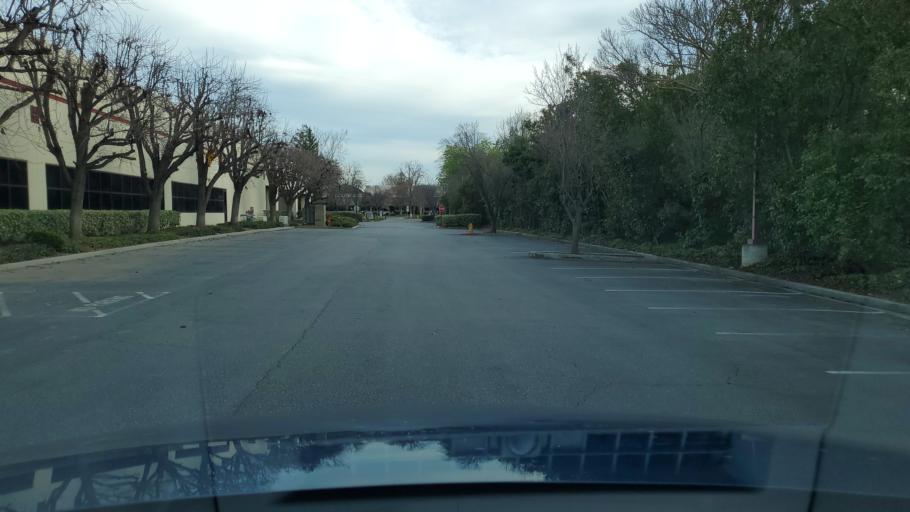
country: US
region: California
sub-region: Santa Clara County
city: Milpitas
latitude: 37.3882
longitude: -121.9043
